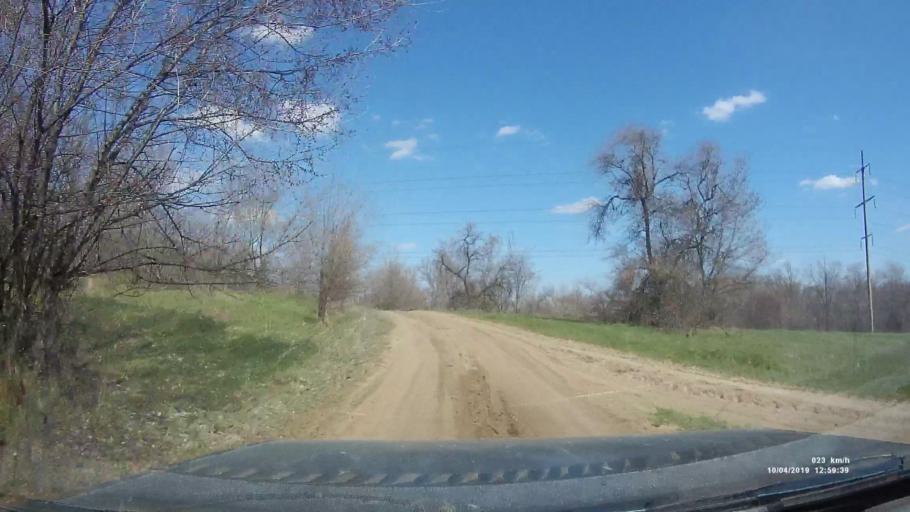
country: RU
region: Rostov
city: Masalovka
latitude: 48.3783
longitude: 40.2285
